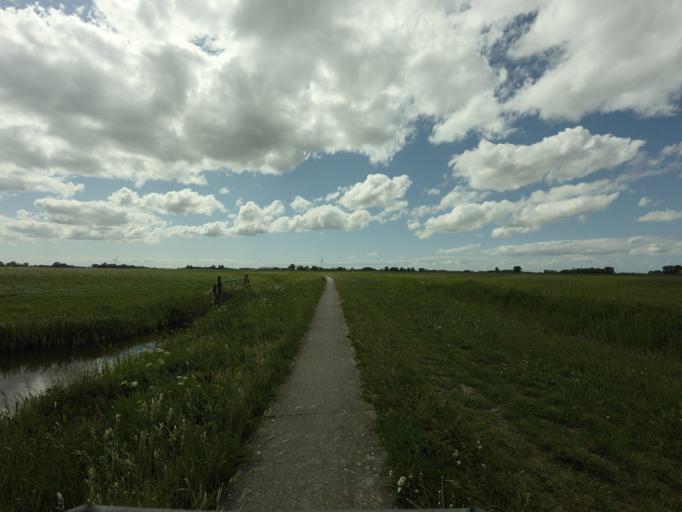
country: NL
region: Friesland
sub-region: Gemeente Littenseradiel
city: Wommels
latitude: 53.1305
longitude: 5.5725
